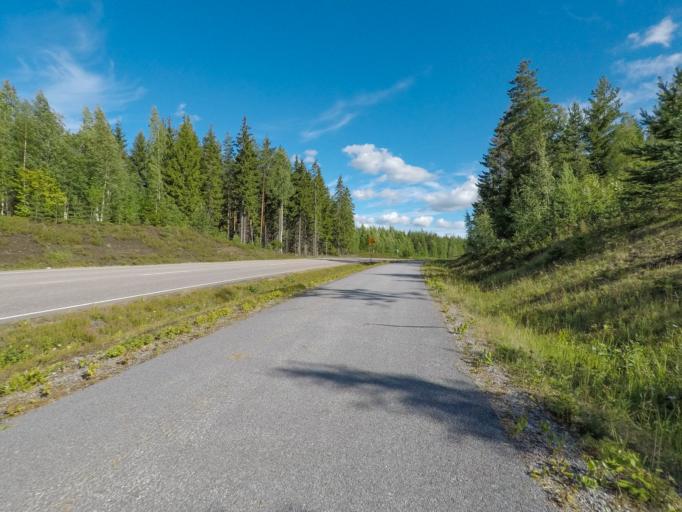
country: FI
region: South Karelia
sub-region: Lappeenranta
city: Joutseno
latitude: 61.1527
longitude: 28.6122
